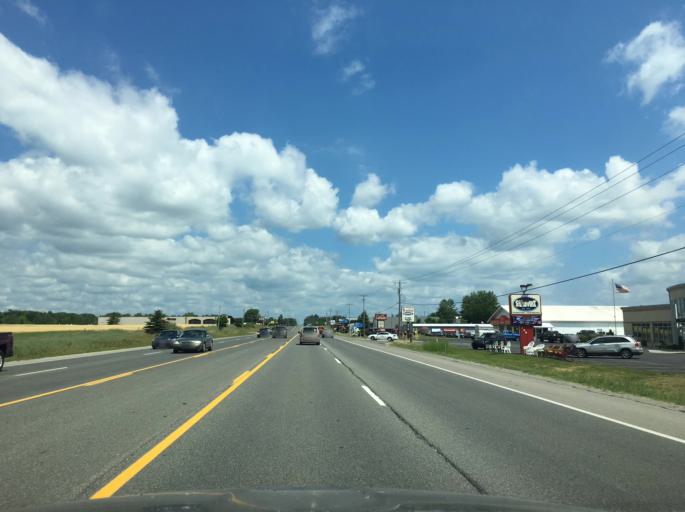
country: US
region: Michigan
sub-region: Grand Traverse County
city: Traverse City
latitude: 44.6923
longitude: -85.6562
